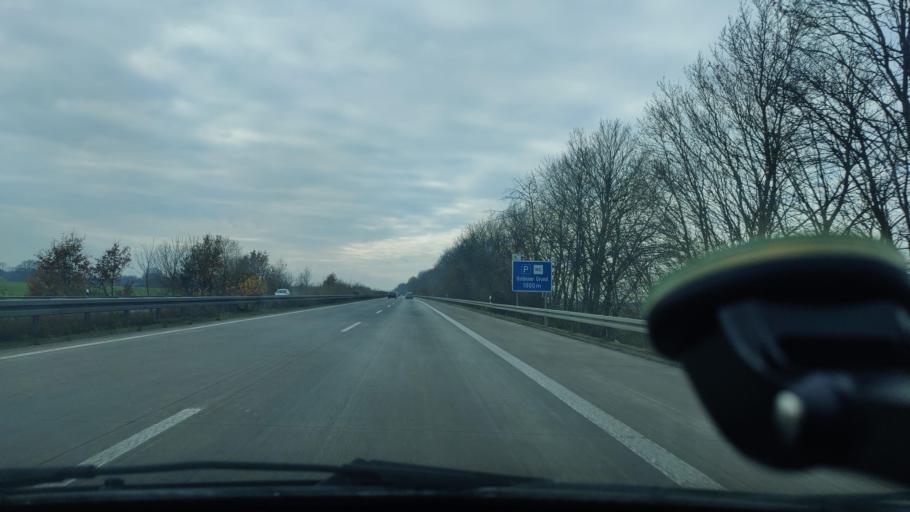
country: DE
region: North Rhine-Westphalia
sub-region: Regierungsbezirk Arnsberg
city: Soest
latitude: 51.5450
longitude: 8.0387
